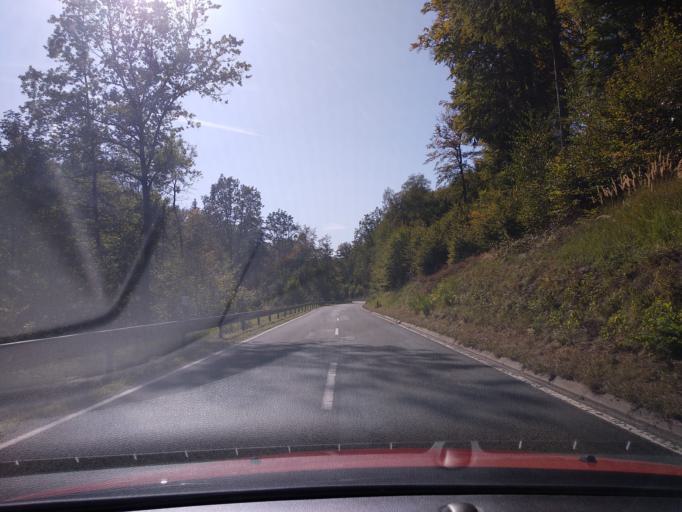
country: DE
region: Lower Saxony
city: Furstenberg
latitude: 51.7527
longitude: 9.4394
